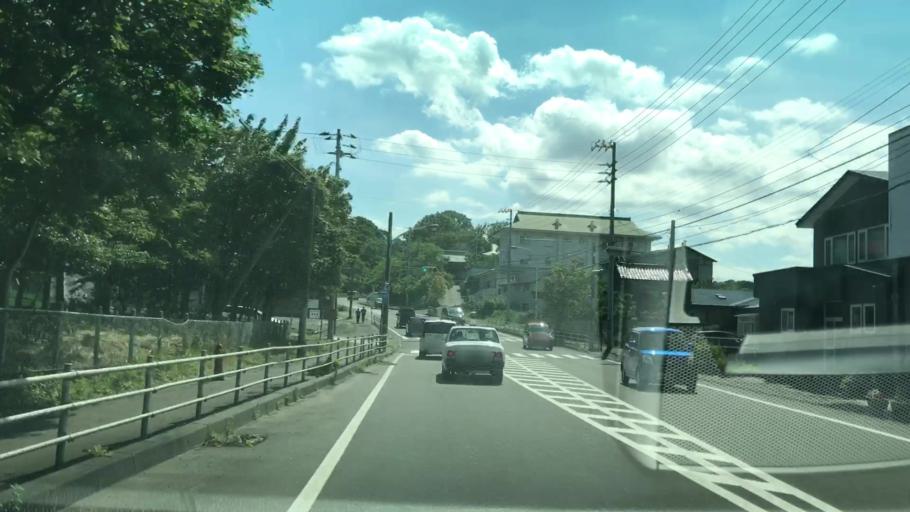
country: JP
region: Hokkaido
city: Muroran
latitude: 42.3198
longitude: 140.9961
